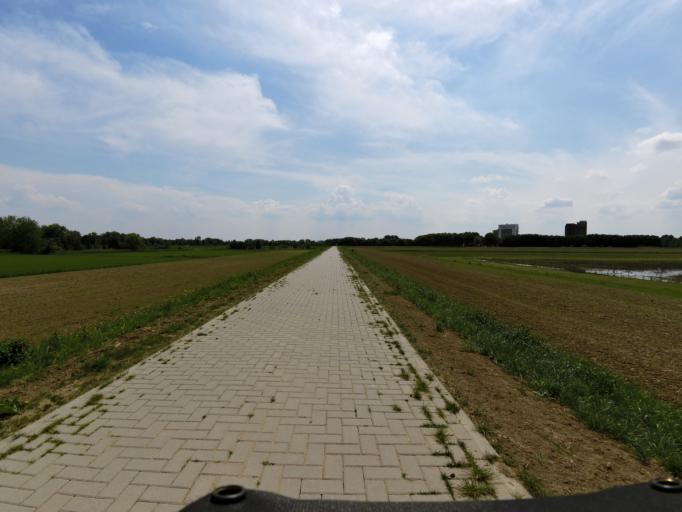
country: NL
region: North Brabant
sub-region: Gemeente Woudrichem
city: Woudrichem
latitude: 51.8034
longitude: 5.0564
